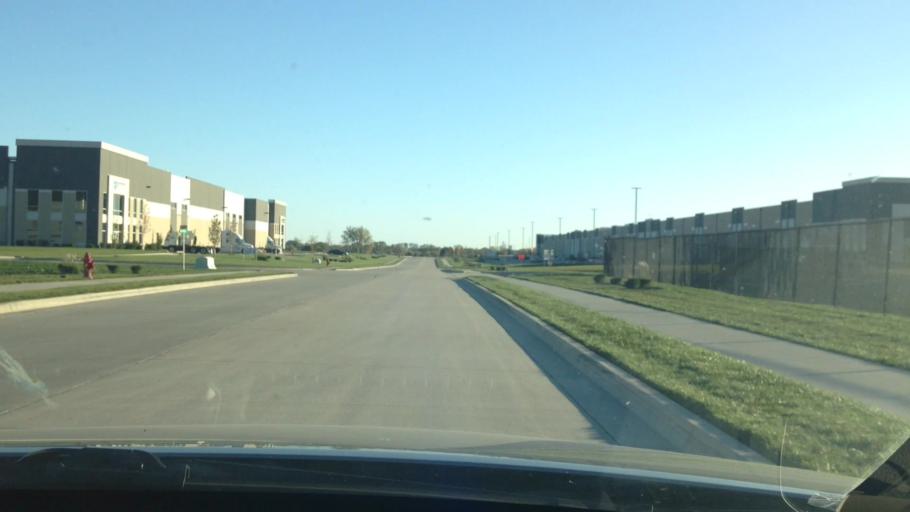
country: US
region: Kansas
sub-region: Johnson County
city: Gardner
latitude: 38.7780
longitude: -94.9423
